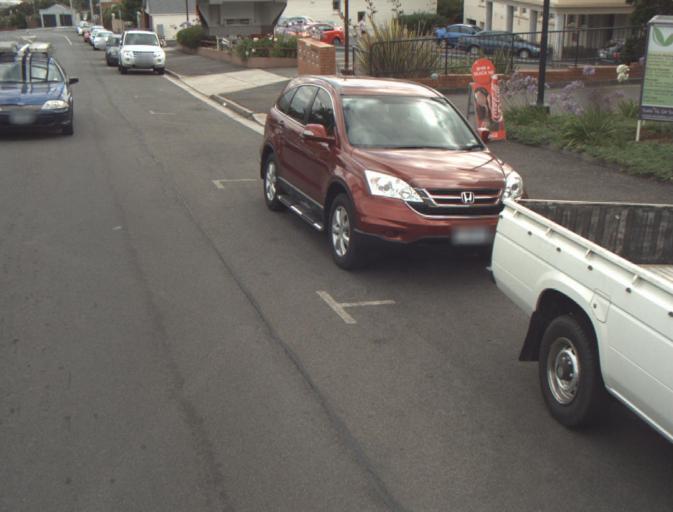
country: AU
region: Tasmania
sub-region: Launceston
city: East Launceston
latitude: -41.4334
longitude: 147.1474
